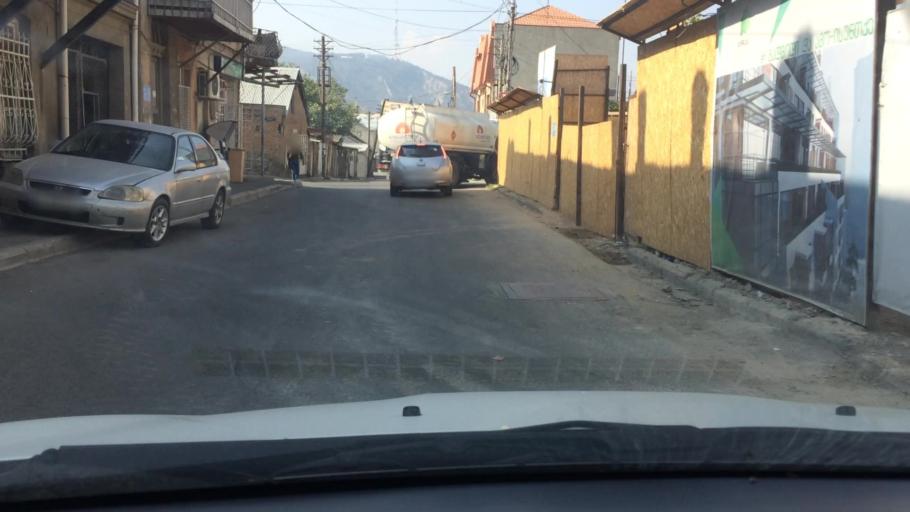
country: GE
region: T'bilisi
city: Tbilisi
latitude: 41.6910
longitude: 44.8251
